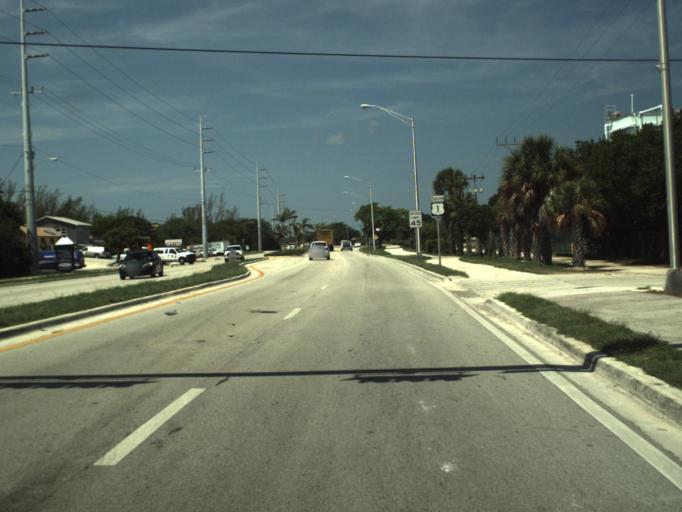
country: US
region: Florida
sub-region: Monroe County
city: Marathon
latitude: 24.7285
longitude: -81.0393
